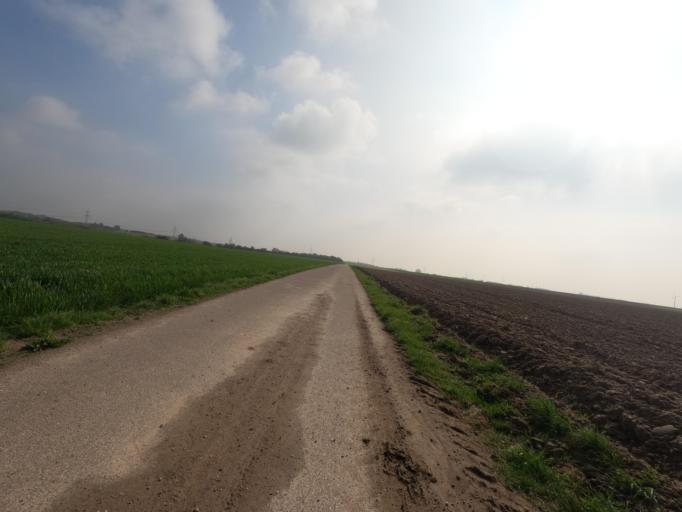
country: DE
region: North Rhine-Westphalia
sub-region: Regierungsbezirk Koln
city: Heinsberg
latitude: 51.0451
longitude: 6.0807
